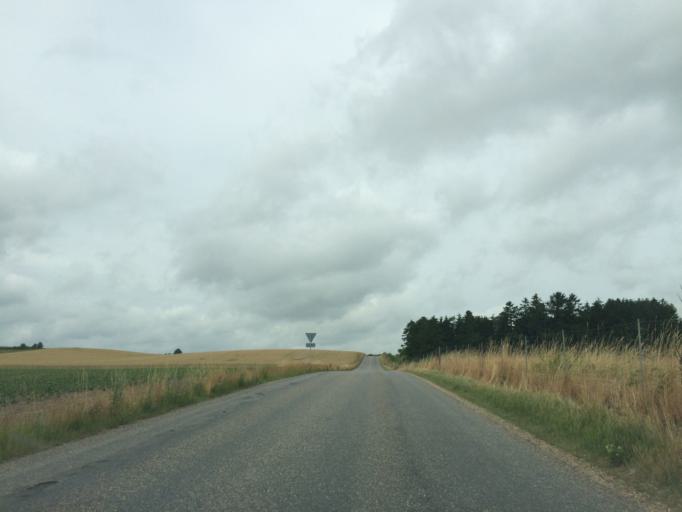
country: DK
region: Central Jutland
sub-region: Silkeborg Kommune
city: Svejbaek
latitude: 56.2270
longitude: 9.6631
